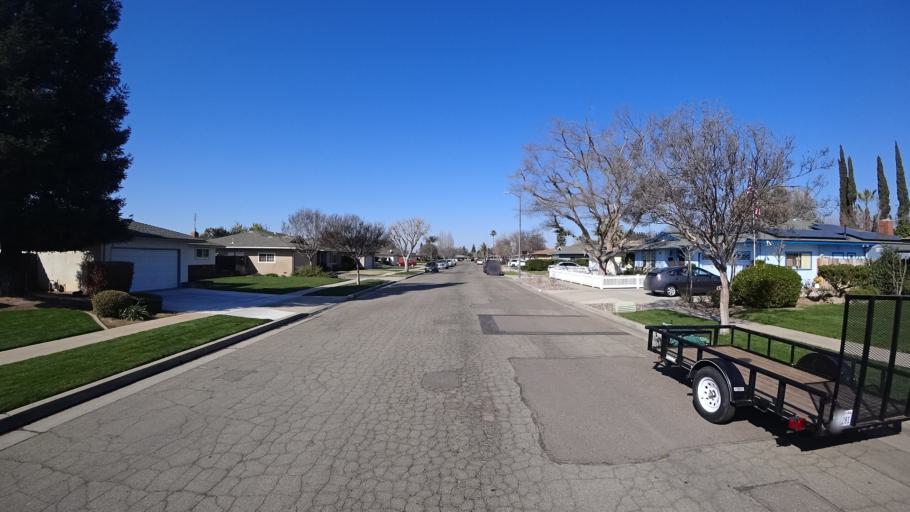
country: US
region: California
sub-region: Fresno County
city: Clovis
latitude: 36.8325
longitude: -119.7427
